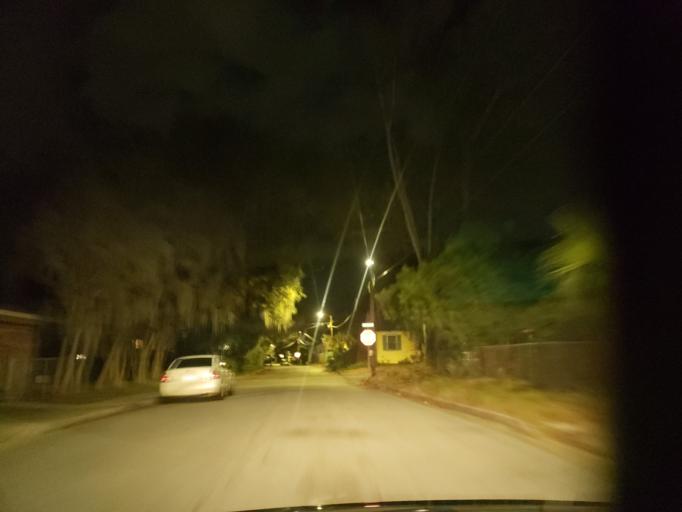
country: US
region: Georgia
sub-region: Chatham County
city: Thunderbolt
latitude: 32.0492
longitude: -81.0608
